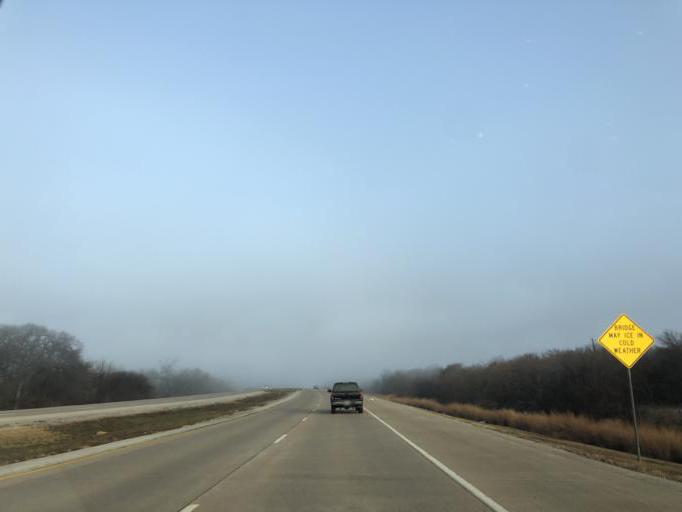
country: US
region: Texas
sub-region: Dallas County
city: Duncanville
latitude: 32.6596
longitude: -96.9811
